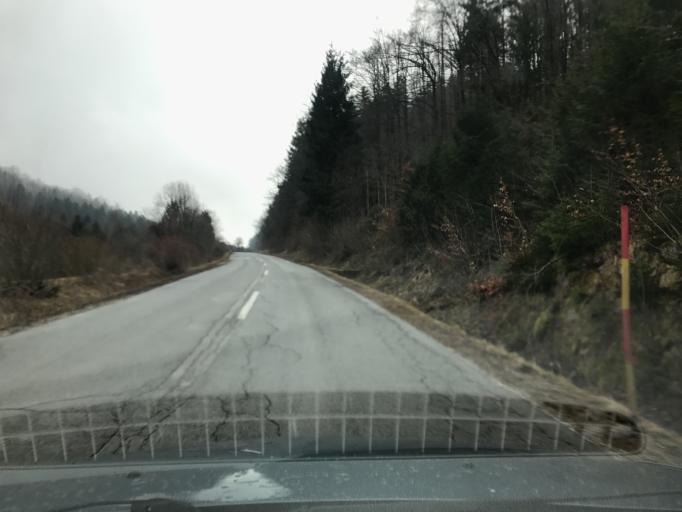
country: SI
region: Gornji Grad
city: Gornji Grad
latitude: 46.2160
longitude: 14.7952
